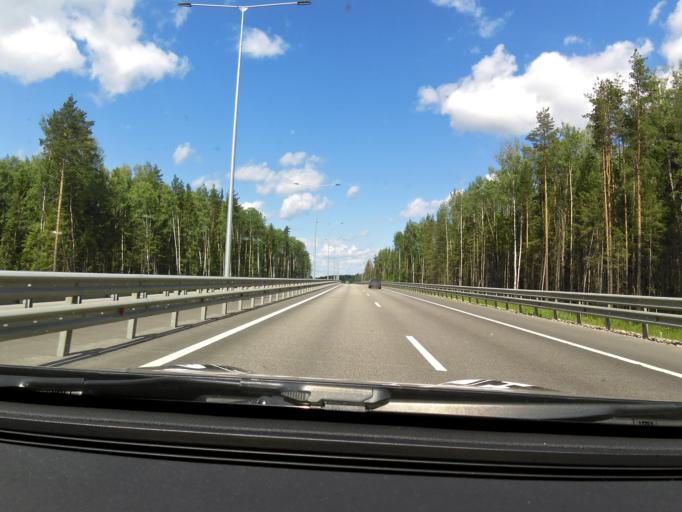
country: RU
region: Tverskaya
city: Vydropuzhsk
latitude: 57.3348
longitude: 34.7340
